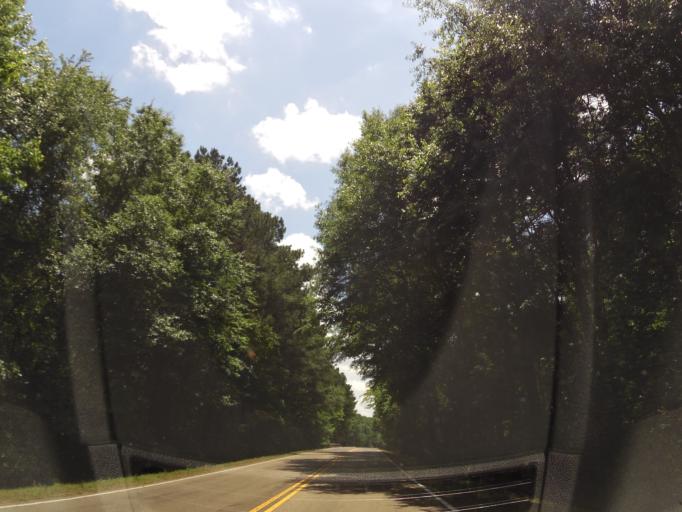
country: US
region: Mississippi
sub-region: Lee County
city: Tupelo
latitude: 34.2947
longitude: -88.7266
